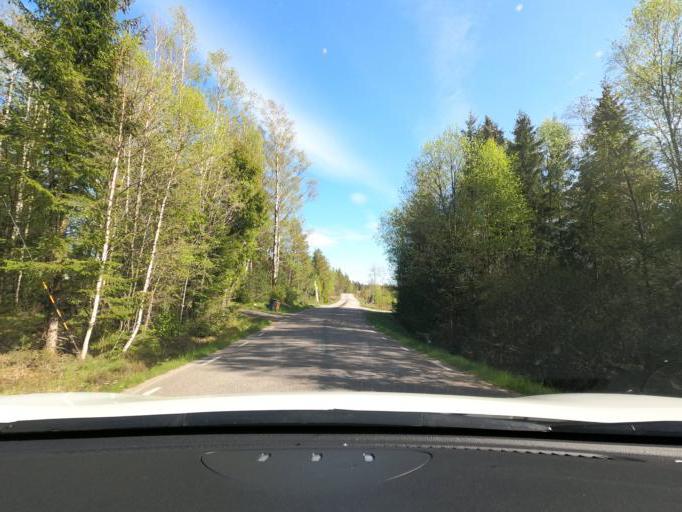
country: SE
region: Vaestra Goetaland
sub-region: Harryda Kommun
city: Hindas
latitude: 57.6620
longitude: 12.3539
